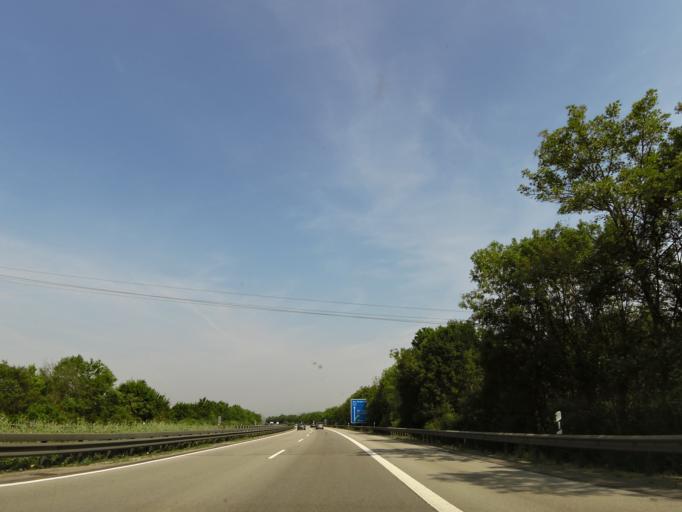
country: DE
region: Rheinland-Pfalz
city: Albig
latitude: 49.7823
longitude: 8.1058
